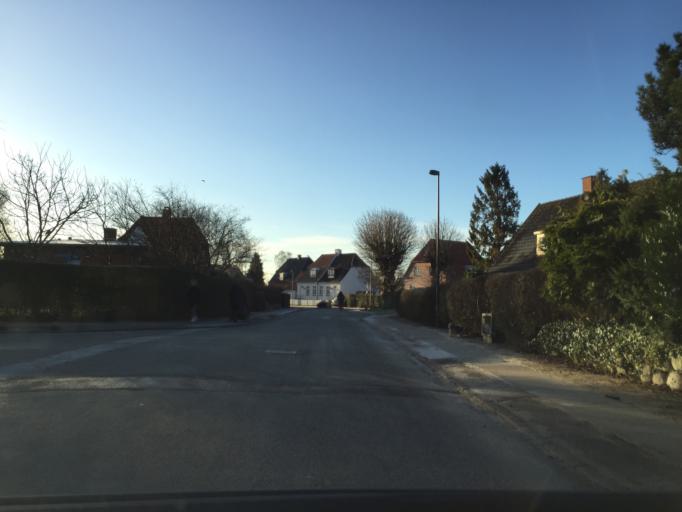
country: DK
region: Capital Region
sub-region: Hvidovre Kommune
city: Hvidovre
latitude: 55.6620
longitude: 12.4969
